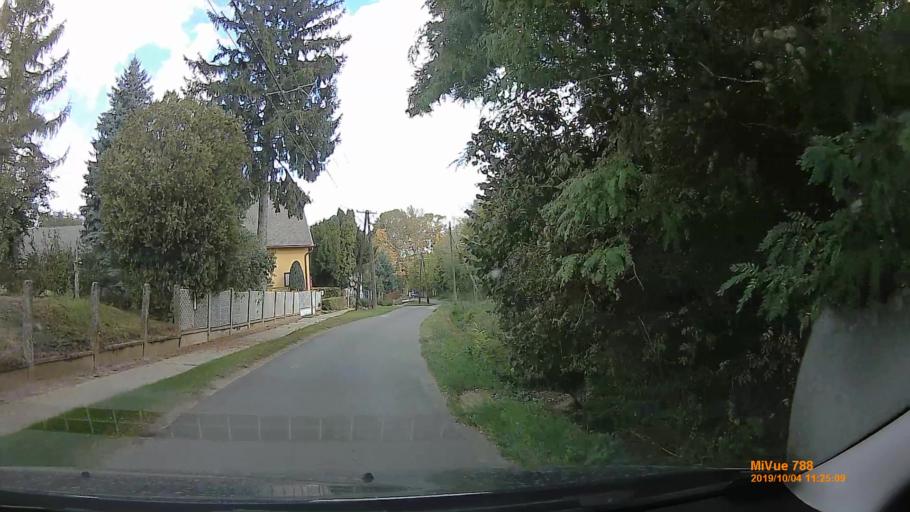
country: HU
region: Somogy
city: Kaposvar
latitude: 46.5050
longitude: 17.8144
